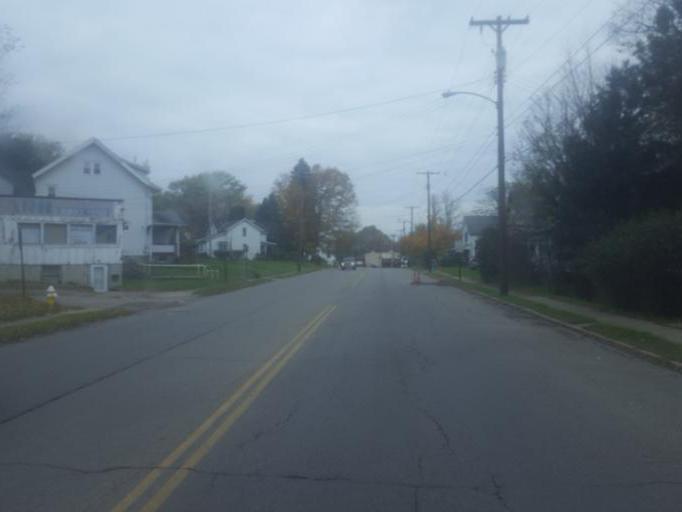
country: US
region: Ohio
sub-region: Richland County
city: Mansfield
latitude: 40.7490
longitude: -82.5103
